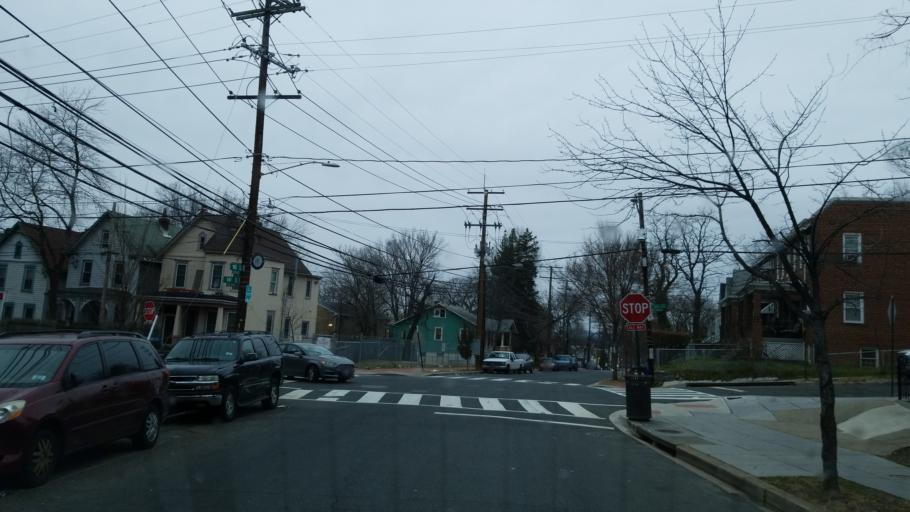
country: US
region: Maryland
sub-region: Prince George's County
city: Hillcrest Heights
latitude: 38.8634
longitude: -76.9827
